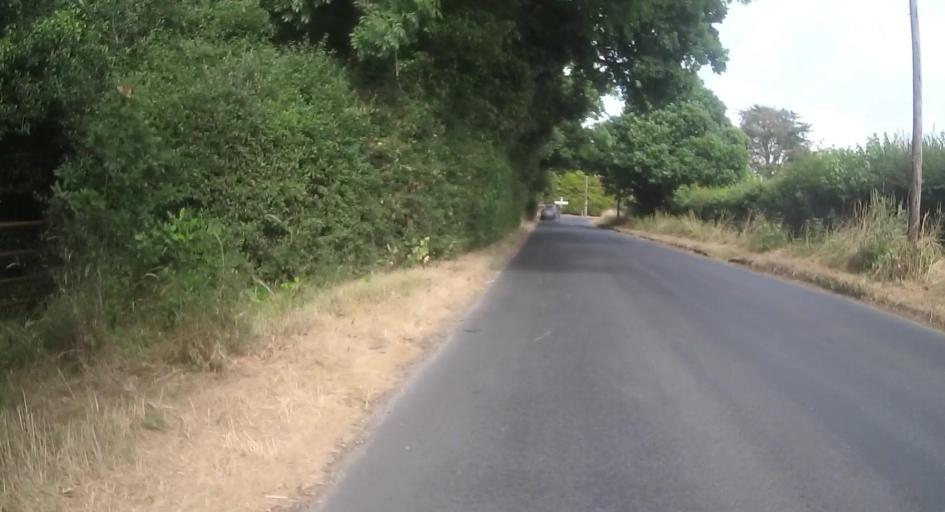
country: GB
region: England
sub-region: Dorset
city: Wareham
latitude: 50.6701
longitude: -2.1151
